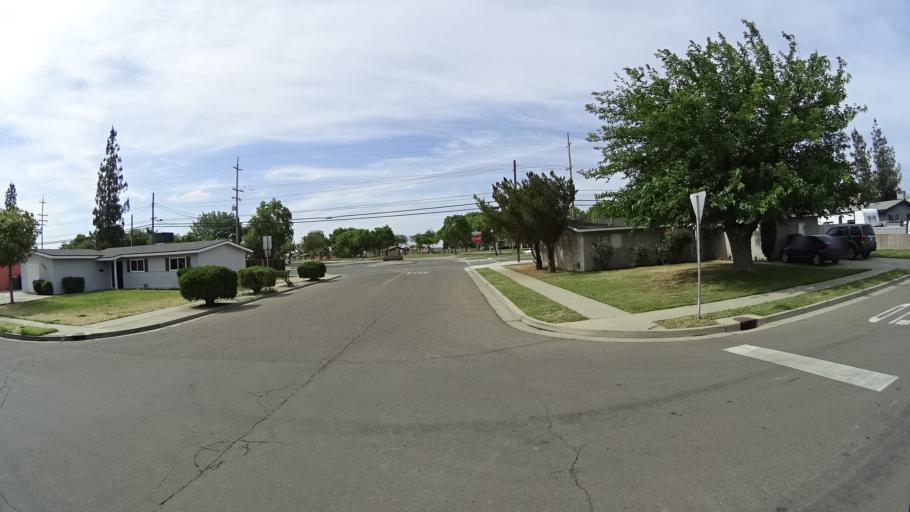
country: US
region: California
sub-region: Kings County
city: Hanford
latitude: 36.3140
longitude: -119.6670
